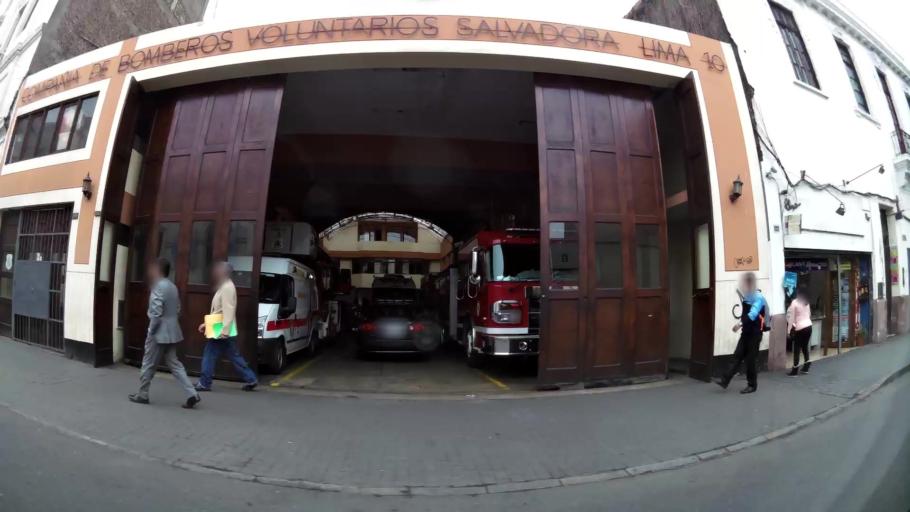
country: PE
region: Lima
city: Lima
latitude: -12.0522
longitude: -77.0356
